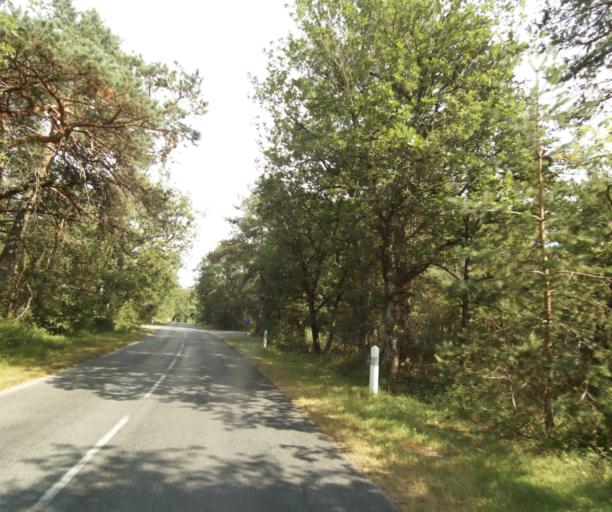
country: FR
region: Ile-de-France
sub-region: Departement de Seine-et-Marne
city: Acheres-la-Foret
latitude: 48.3709
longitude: 2.5610
